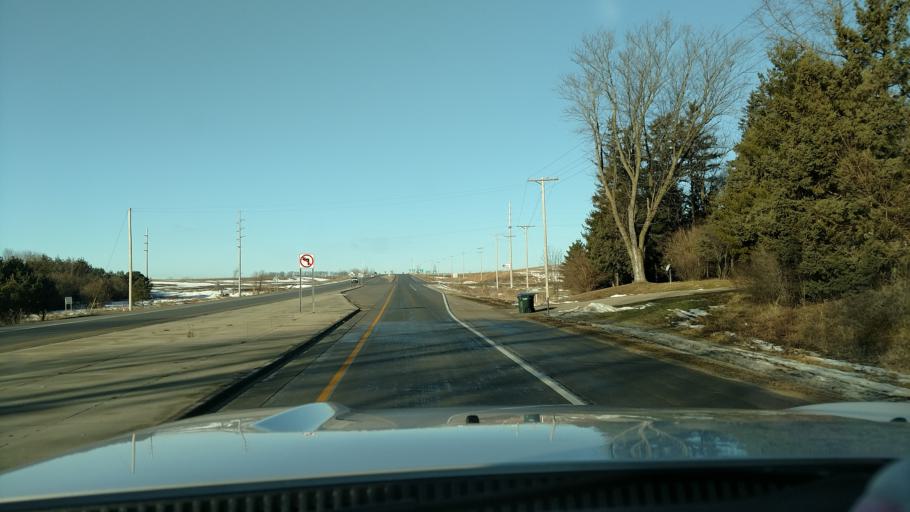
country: US
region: Minnesota
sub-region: Olmsted County
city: Oronoco
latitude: 44.1082
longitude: -92.5059
